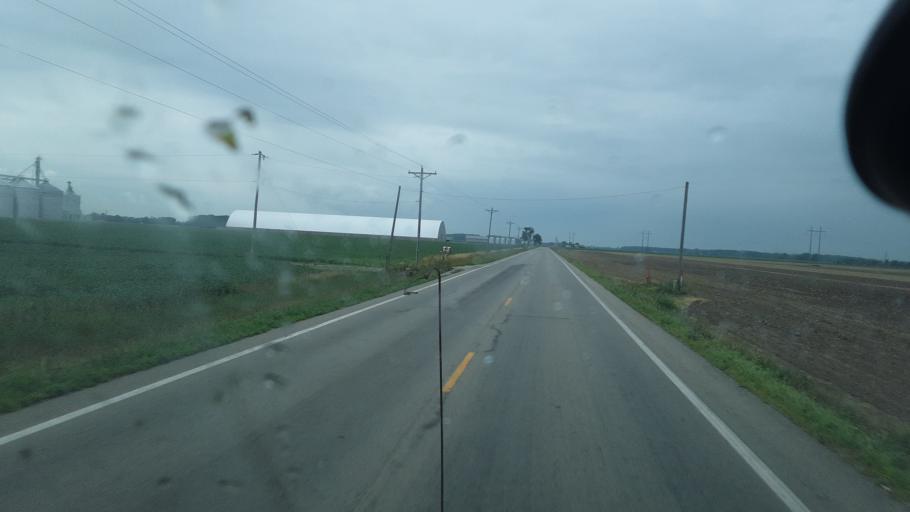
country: US
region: Ohio
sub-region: Defiance County
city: Hicksville
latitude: 41.2962
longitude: -84.6975
